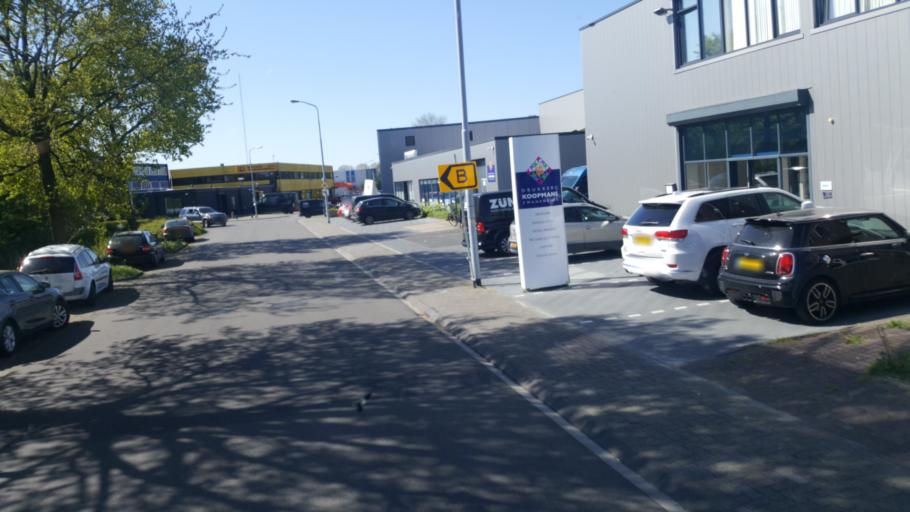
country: NL
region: North Holland
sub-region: Gemeente Haarlemmermeer
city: Hoofddorp
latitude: 52.3826
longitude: 4.7387
